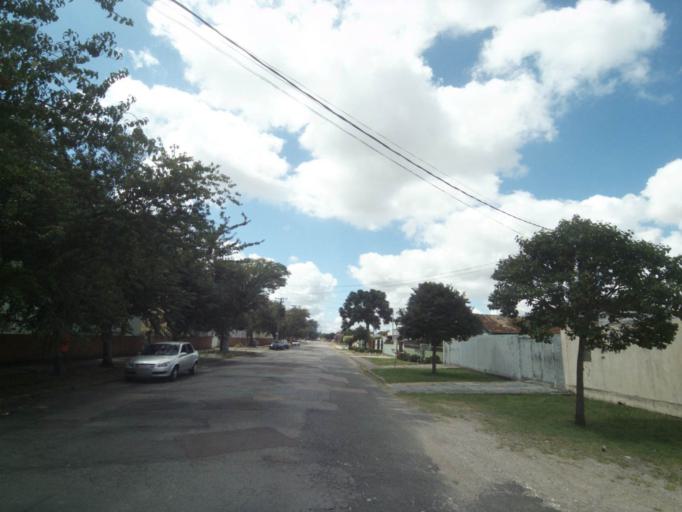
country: BR
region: Parana
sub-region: Pinhais
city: Pinhais
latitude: -25.4411
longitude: -49.2109
